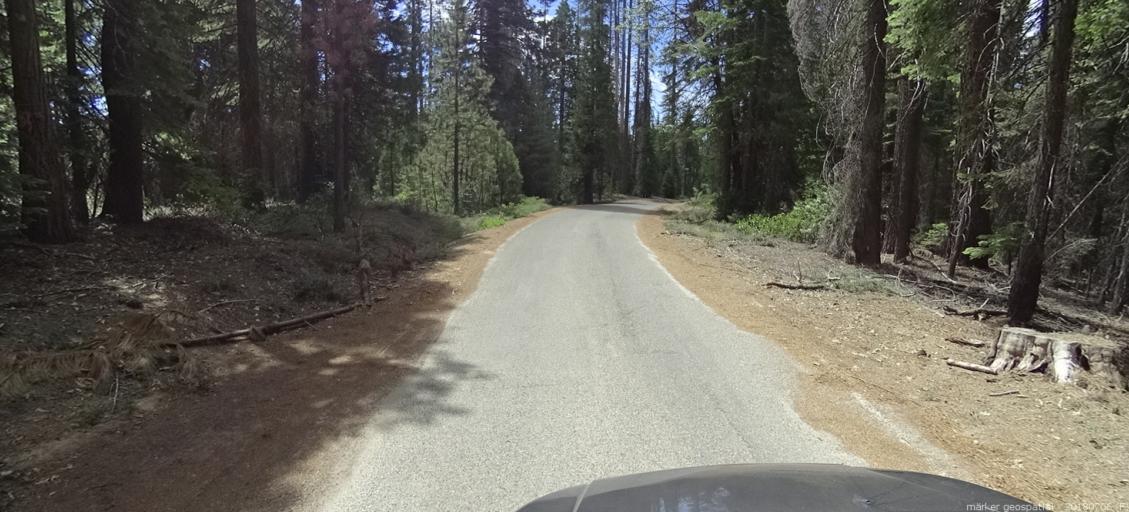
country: US
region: California
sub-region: Madera County
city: Oakhurst
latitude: 37.4078
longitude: -119.4113
